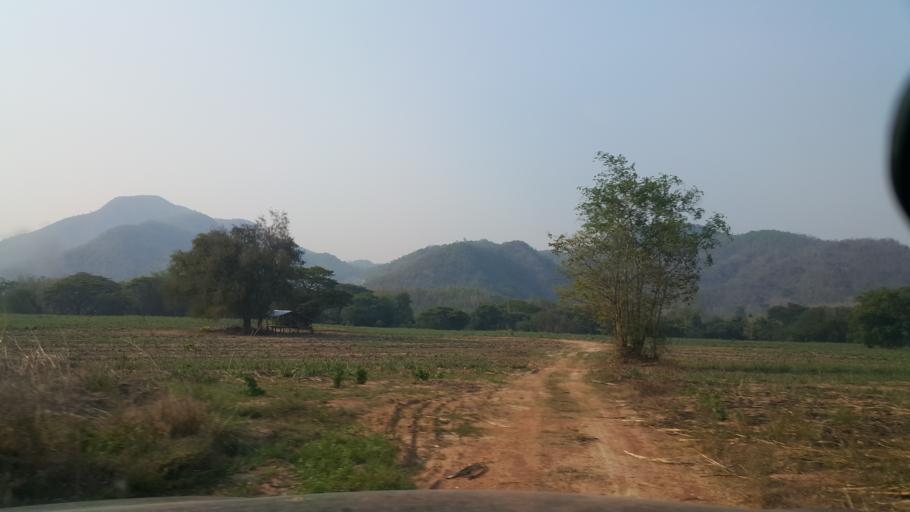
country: TH
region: Sukhothai
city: Thung Saliam
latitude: 17.3385
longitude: 99.4682
